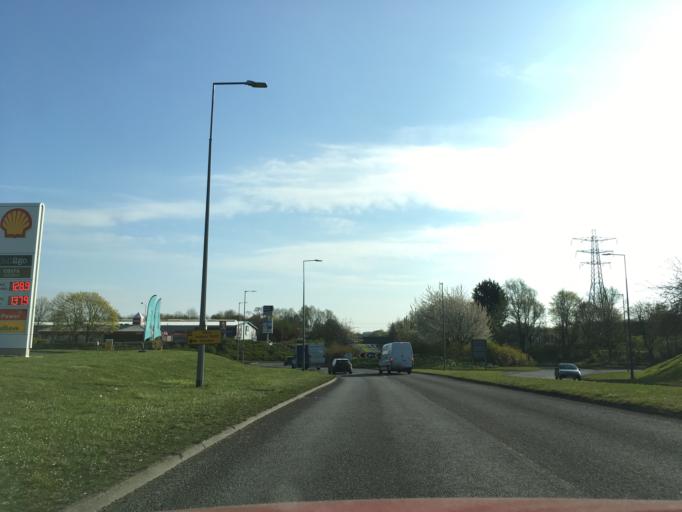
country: GB
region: England
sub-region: Milton Keynes
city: Bradwell
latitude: 52.0493
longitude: -0.7995
